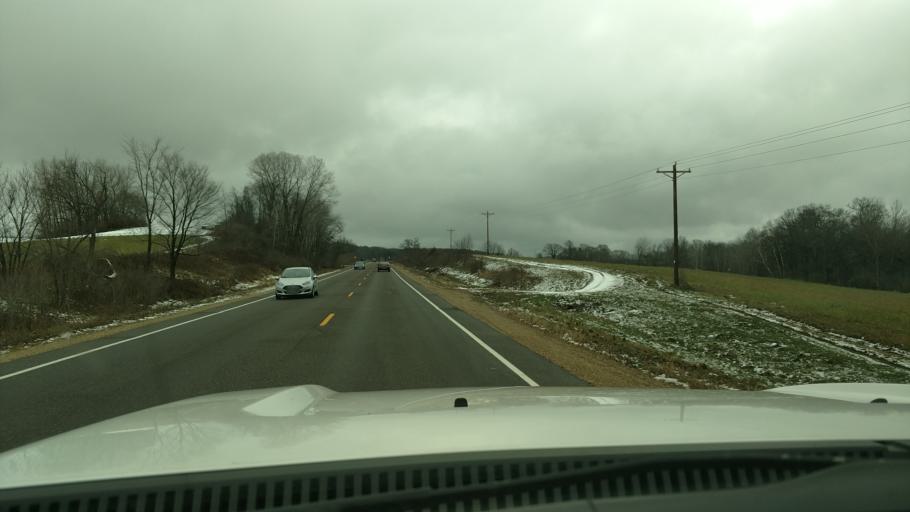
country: US
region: Wisconsin
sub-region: Dunn County
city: Boyceville
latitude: 45.1391
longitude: -91.9613
